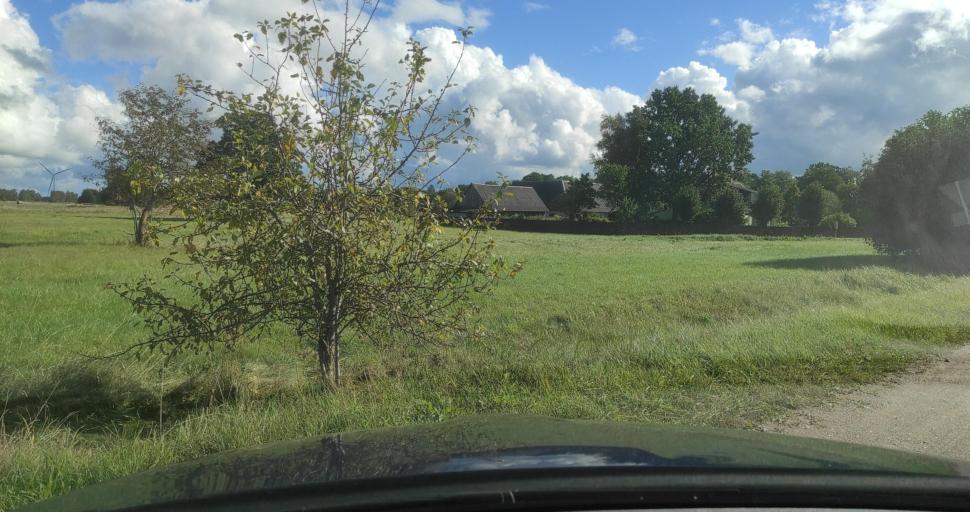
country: LV
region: Ventspils
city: Ventspils
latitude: 57.3699
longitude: 21.6312
